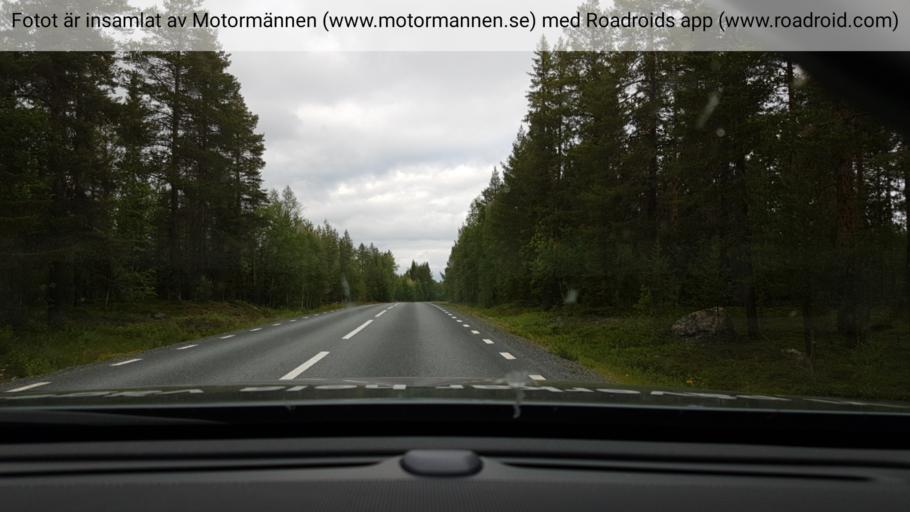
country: SE
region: Vaesterbotten
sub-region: Sorsele Kommun
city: Sorsele
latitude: 65.4299
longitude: 17.5730
